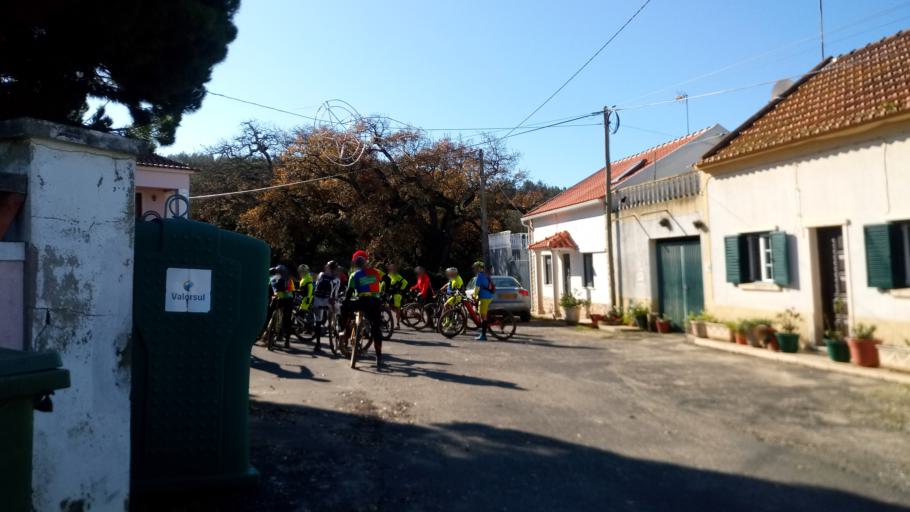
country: PT
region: Leiria
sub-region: Caldas da Rainha
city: Caldas da Rainha
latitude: 39.3920
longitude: -9.0833
